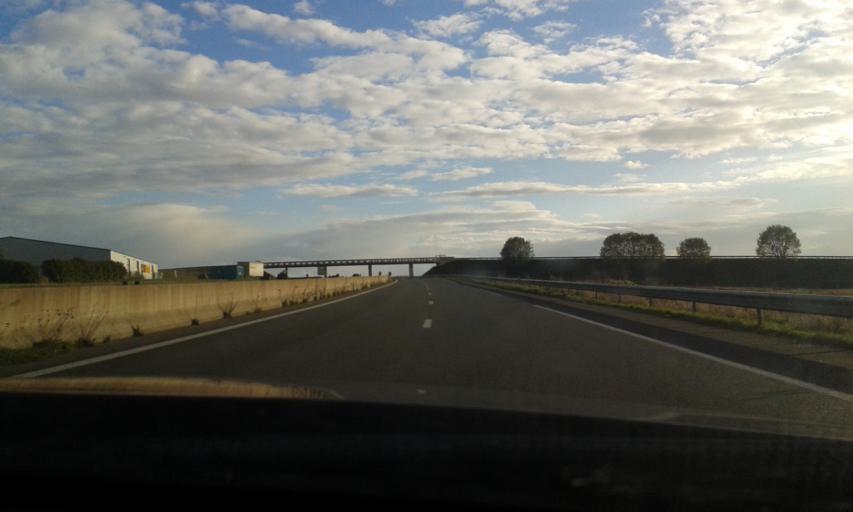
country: FR
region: Centre
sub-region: Departement d'Eure-et-Loir
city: Villemeux-sur-Eure
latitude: 48.5990
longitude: 1.4228
